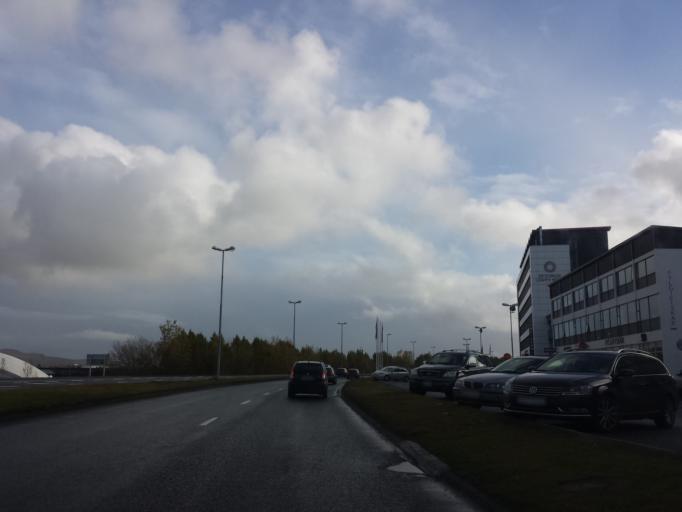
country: IS
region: Capital Region
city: Reykjavik
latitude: 64.1401
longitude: -21.8848
